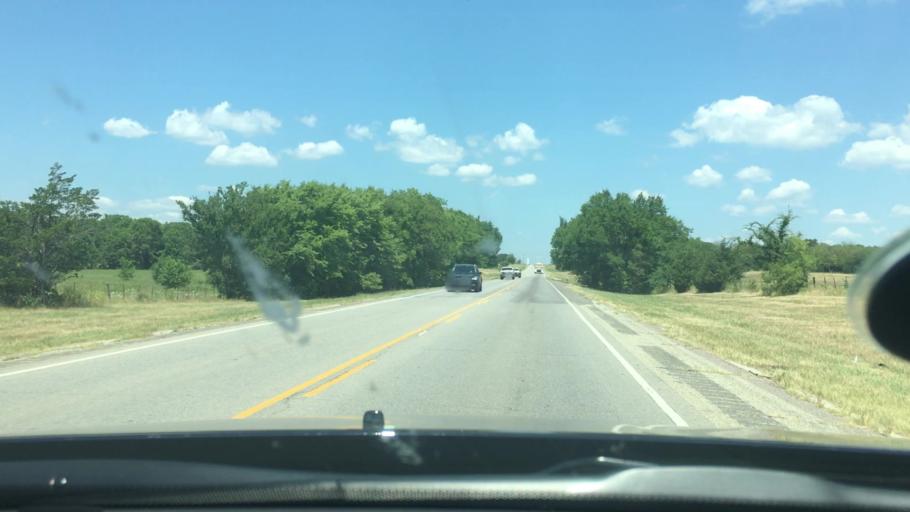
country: US
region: Oklahoma
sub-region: Marshall County
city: Oakland
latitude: 34.1225
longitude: -96.7825
